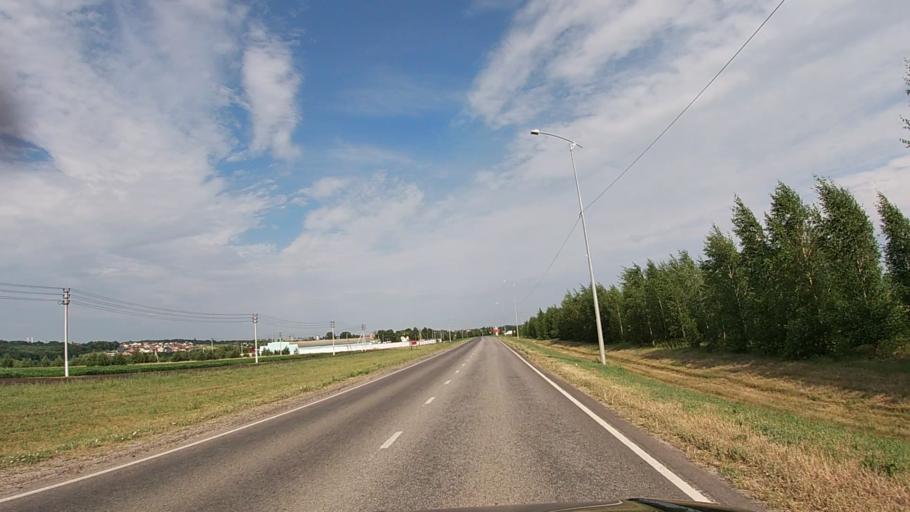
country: RU
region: Belgorod
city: Krasnaya Yaruga
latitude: 50.7978
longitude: 35.6844
